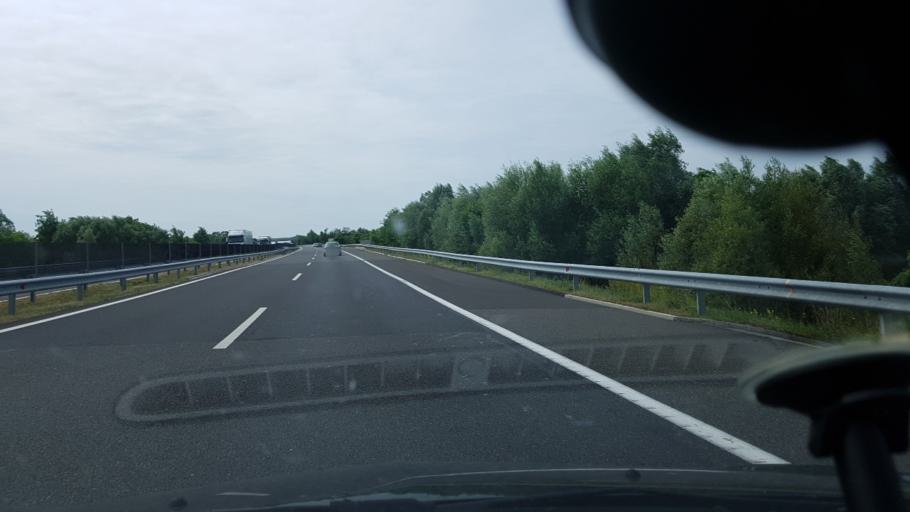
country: HU
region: Somogy
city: Balatonbereny
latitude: 46.6199
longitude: 17.2651
